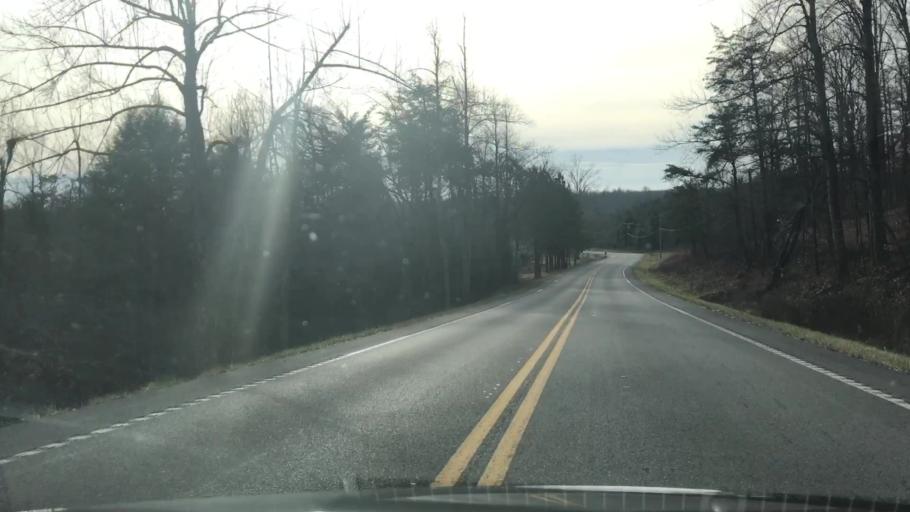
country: US
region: Tennessee
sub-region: Putnam County
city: Monterey
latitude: 36.1271
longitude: -85.2010
